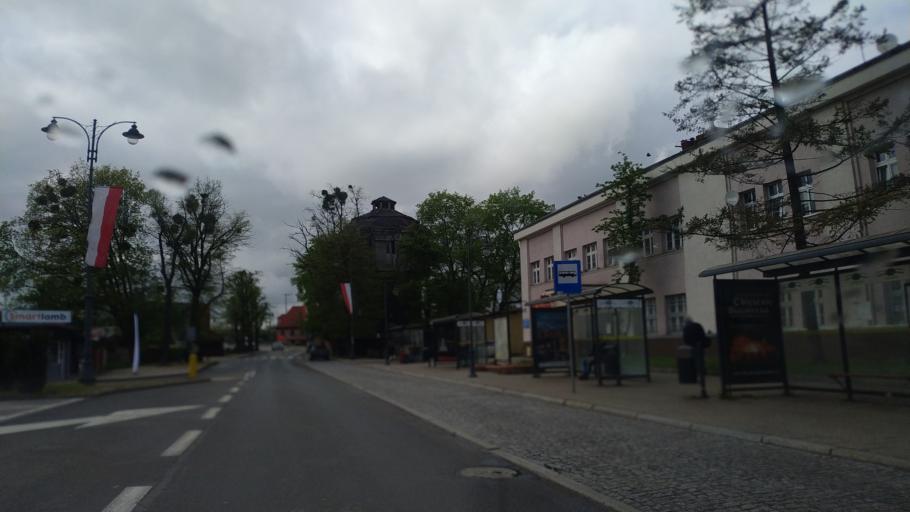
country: PL
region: Pomeranian Voivodeship
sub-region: Powiat malborski
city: Malbork
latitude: 54.0359
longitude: 19.0418
